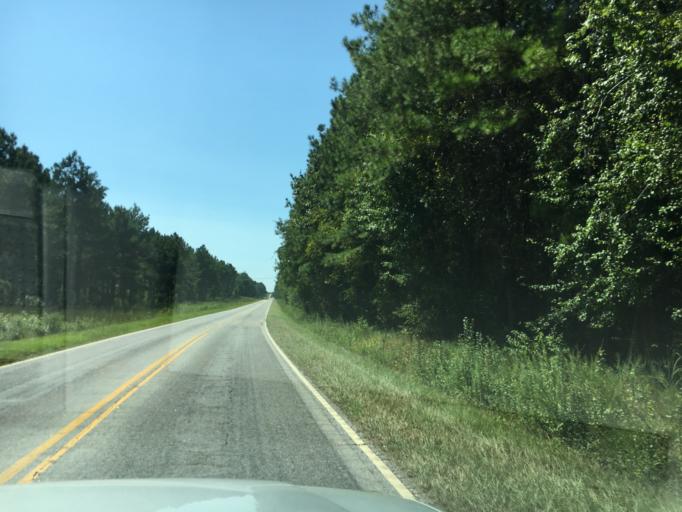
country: US
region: South Carolina
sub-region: Laurens County
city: Joanna
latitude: 34.3115
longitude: -81.8431
